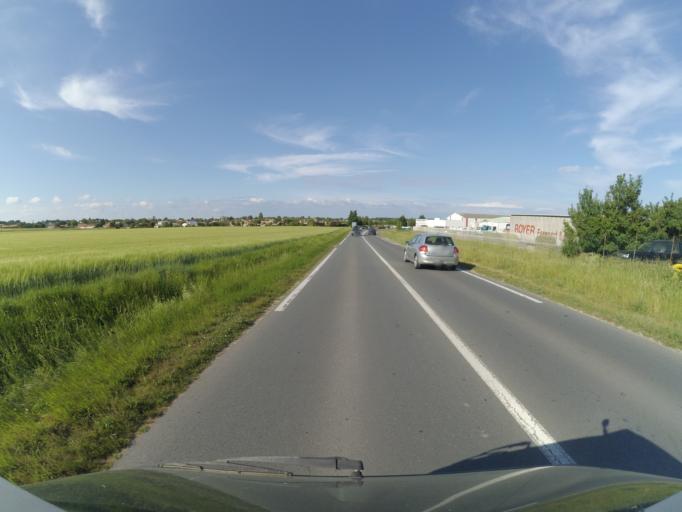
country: FR
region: Poitou-Charentes
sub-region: Departement de la Charente-Maritime
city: Saint-Sulpice-de-Royan
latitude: 45.6633
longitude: -1.0155
